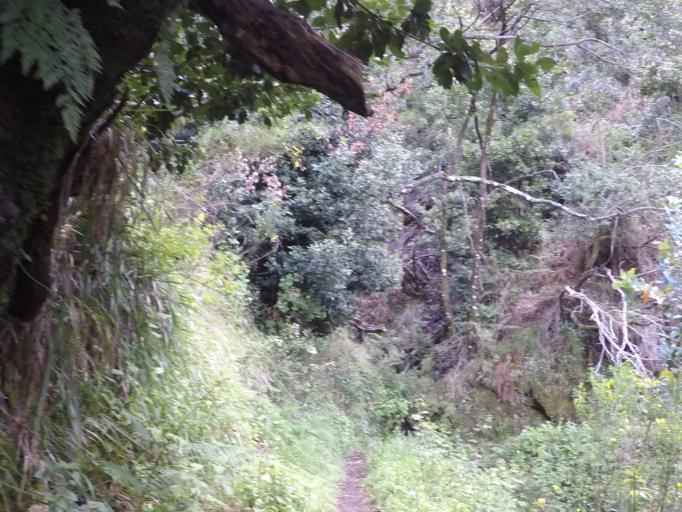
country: PT
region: Madeira
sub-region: Camara de Lobos
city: Curral das Freiras
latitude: 32.7470
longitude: -17.0027
